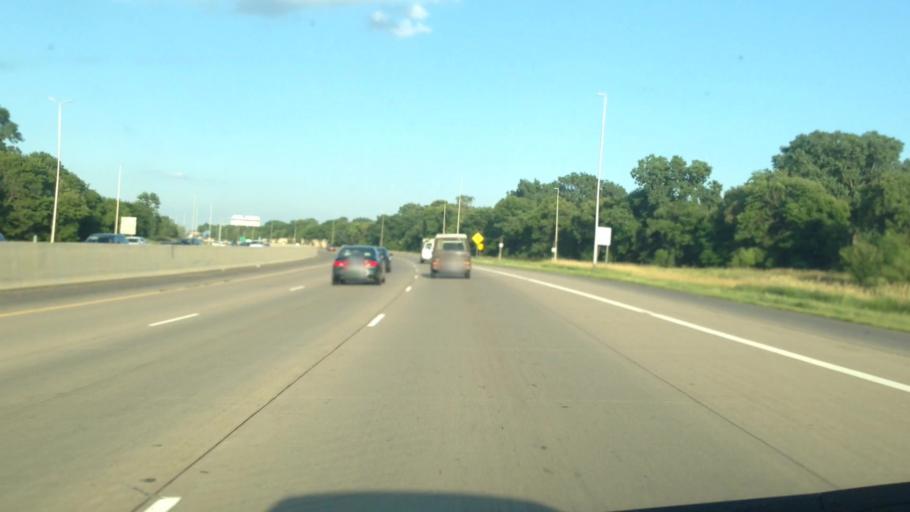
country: US
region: Minnesota
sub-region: Hennepin County
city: Brooklyn Park
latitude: 45.0792
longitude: -93.3905
